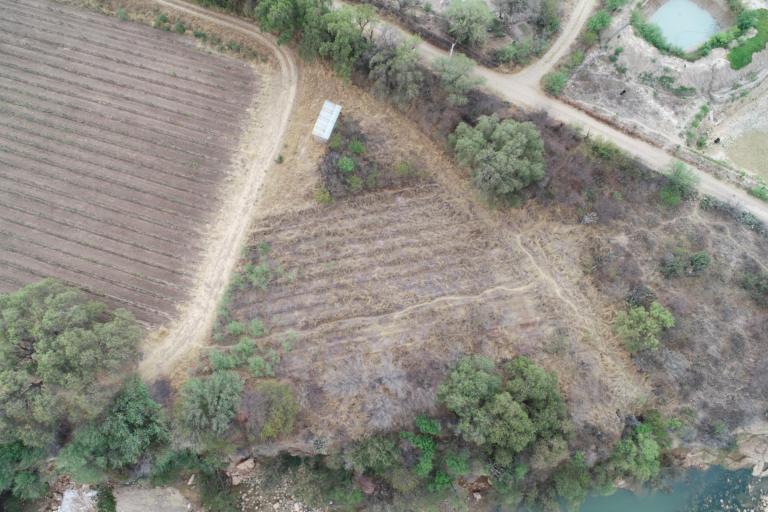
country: BO
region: Tarija
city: Tarija
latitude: -21.6019
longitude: -64.6196
